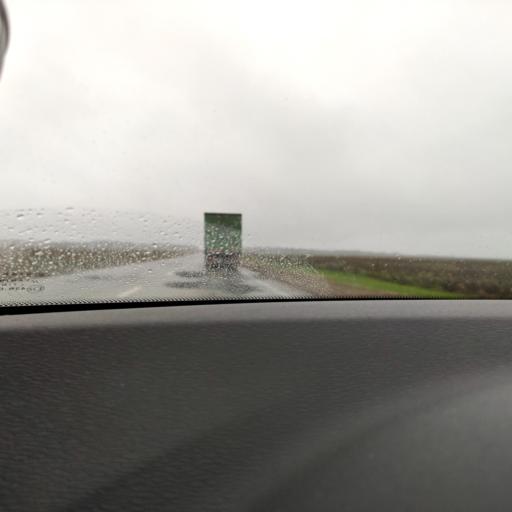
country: RU
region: Samara
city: Yelkhovka
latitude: 53.7161
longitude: 50.2311
